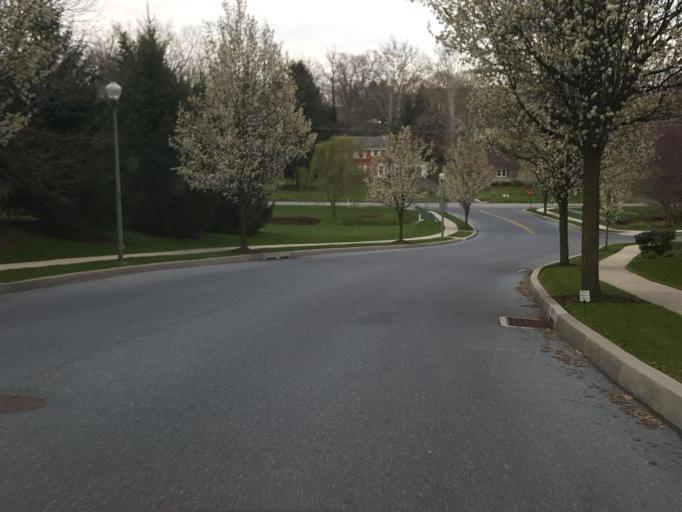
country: US
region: Pennsylvania
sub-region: Dauphin County
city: Middletown
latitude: 40.2309
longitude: -76.7225
